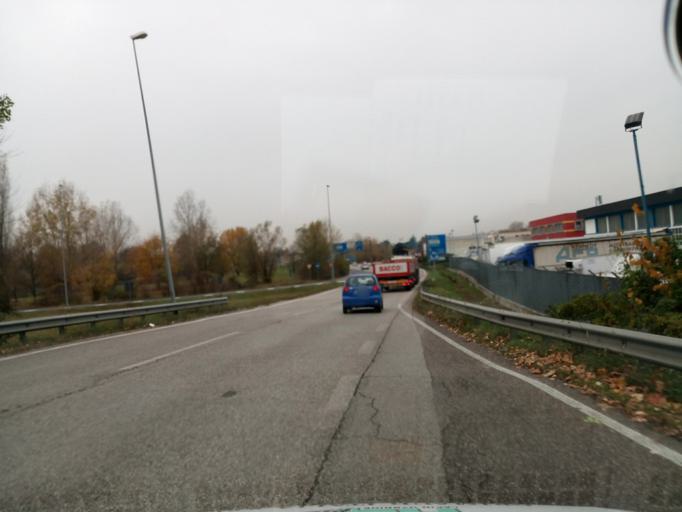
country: IT
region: Veneto
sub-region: Provincia di Padova
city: San Vito
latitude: 45.4323
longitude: 11.9578
